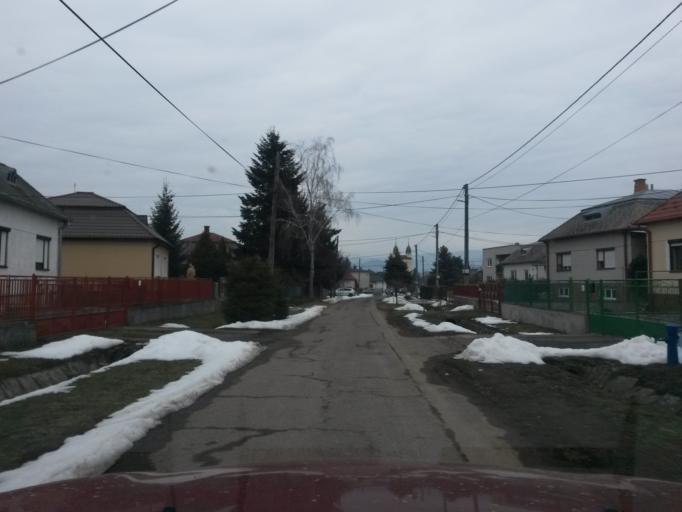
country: SK
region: Kosicky
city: Vinne
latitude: 48.7587
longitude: 21.9936
